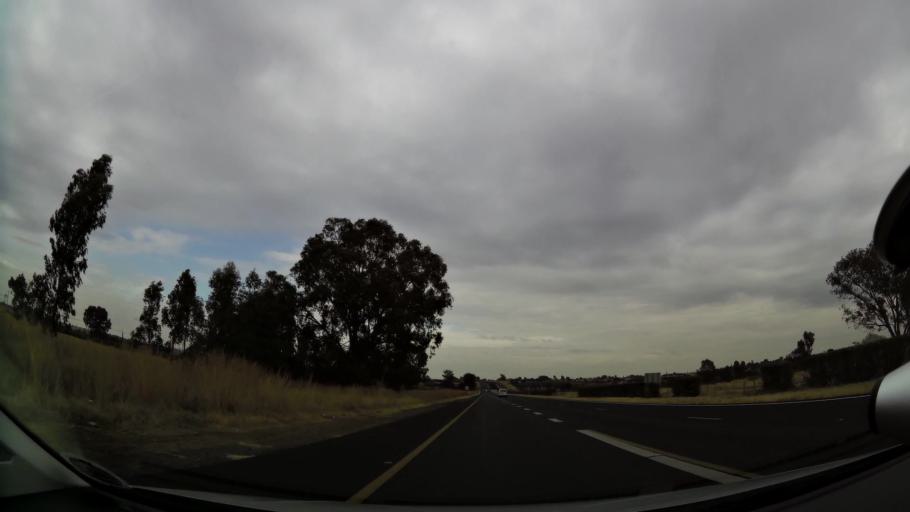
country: ZA
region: Orange Free State
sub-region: Fezile Dabi District Municipality
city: Kroonstad
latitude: -27.6297
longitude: 27.2515
